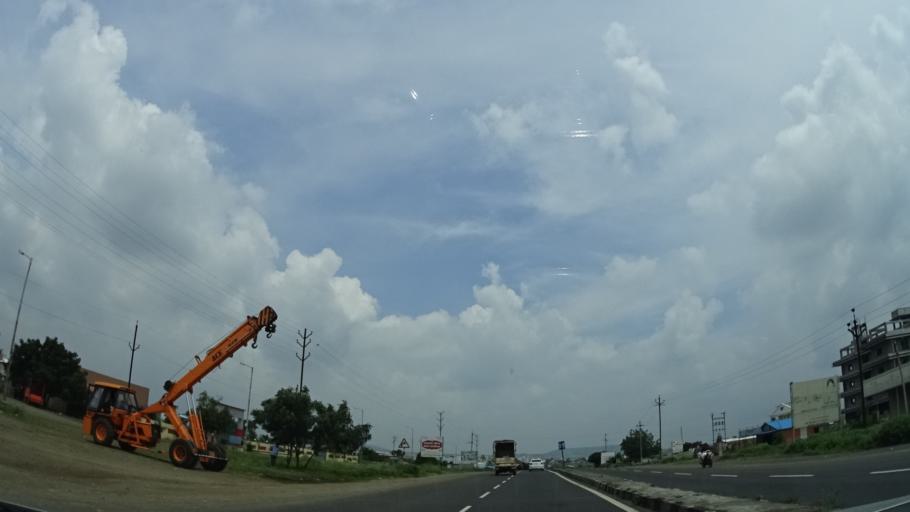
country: IN
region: Maharashtra
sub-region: Pune Division
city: Sirur
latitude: 18.9509
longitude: 74.5203
